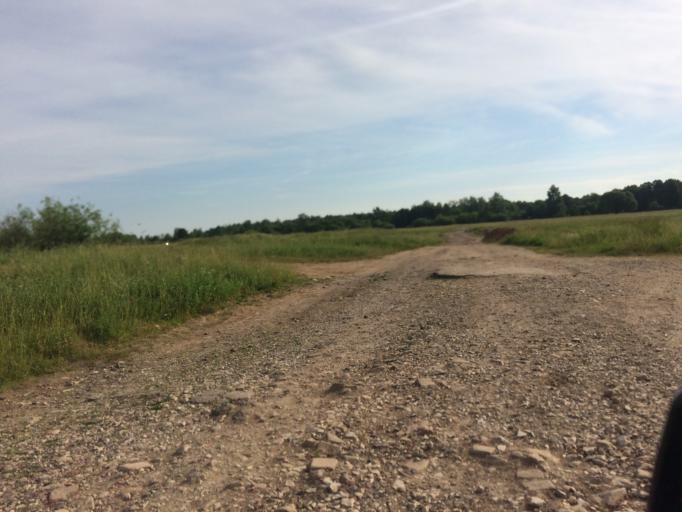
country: RU
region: Mariy-El
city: Yoshkar-Ola
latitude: 56.6542
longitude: 47.9203
